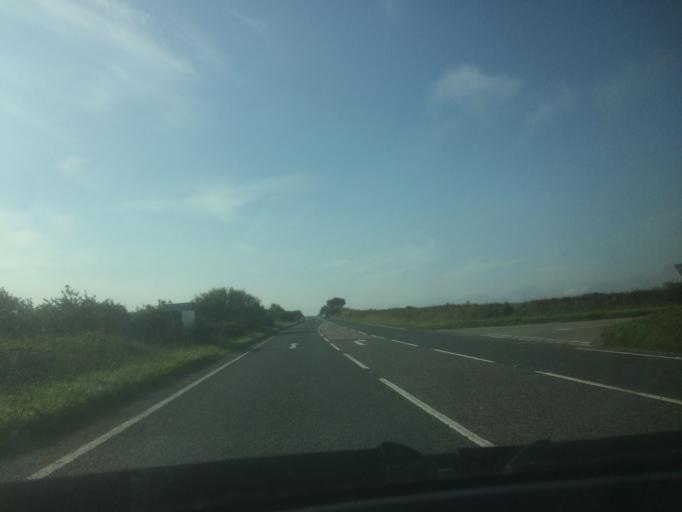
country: GB
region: England
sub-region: Cornwall
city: Callington
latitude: 50.4881
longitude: -4.2875
